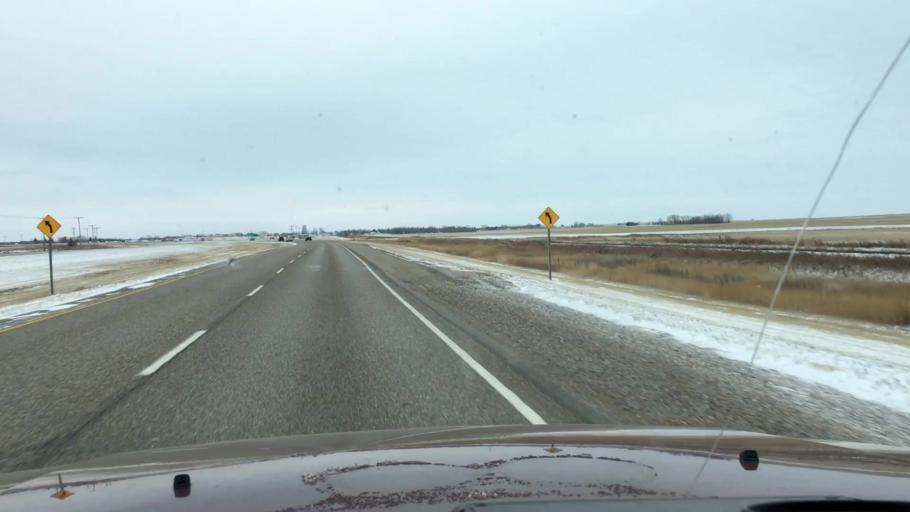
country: CA
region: Saskatchewan
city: Watrous
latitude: 51.0698
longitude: -105.8391
